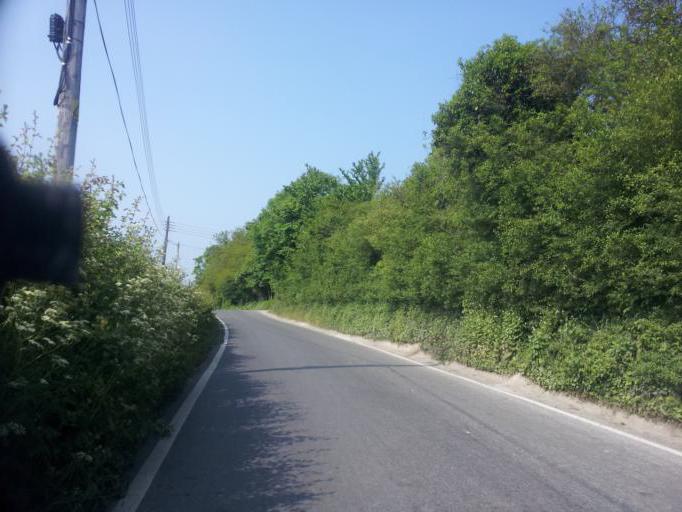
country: GB
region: England
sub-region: Medway
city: Halling
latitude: 51.3509
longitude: 0.4711
